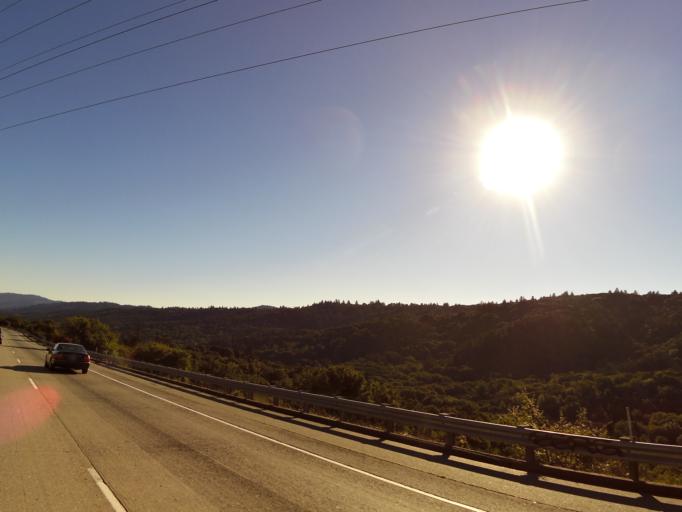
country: US
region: California
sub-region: San Mateo County
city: Hillsborough
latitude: 37.5758
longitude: -122.4013
